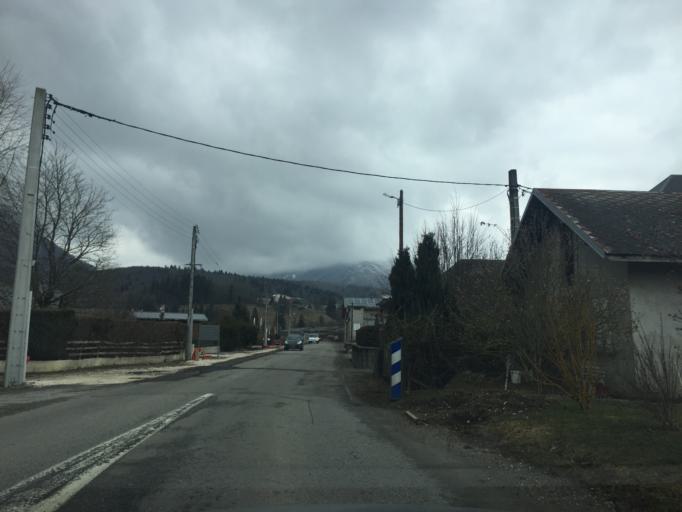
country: FR
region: Rhone-Alpes
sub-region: Departement de la Haute-Savoie
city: Gruffy
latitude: 45.7164
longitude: 6.1073
